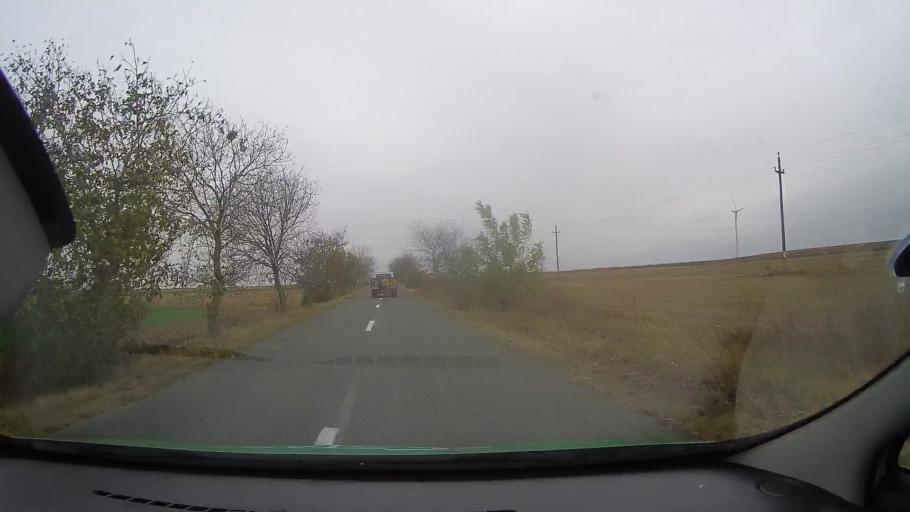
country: RO
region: Constanta
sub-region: Comuna Targusor
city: Targusor
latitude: 44.4779
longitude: 28.3772
